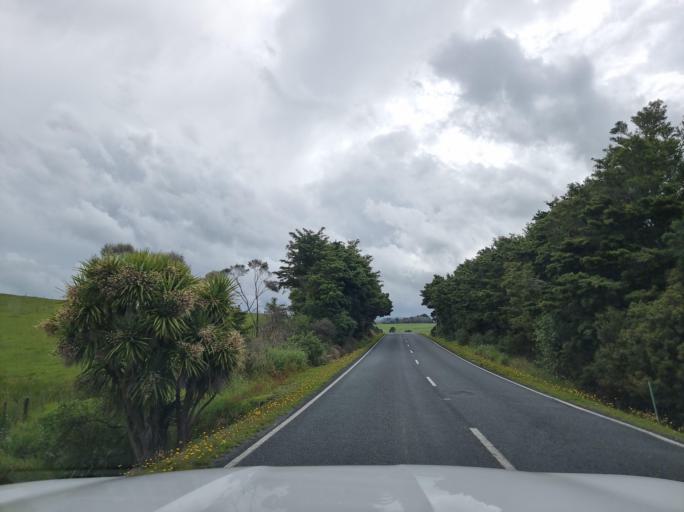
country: NZ
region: Northland
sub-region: Whangarei
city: Ruakaka
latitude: -35.9240
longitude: 174.2792
